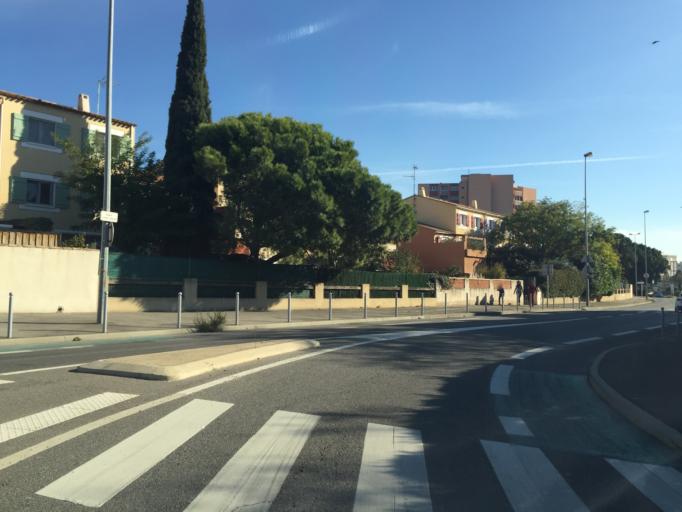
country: FR
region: Provence-Alpes-Cote d'Azur
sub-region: Departement des Bouches-du-Rhone
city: Salon-de-Provence
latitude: 43.6553
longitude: 5.0975
